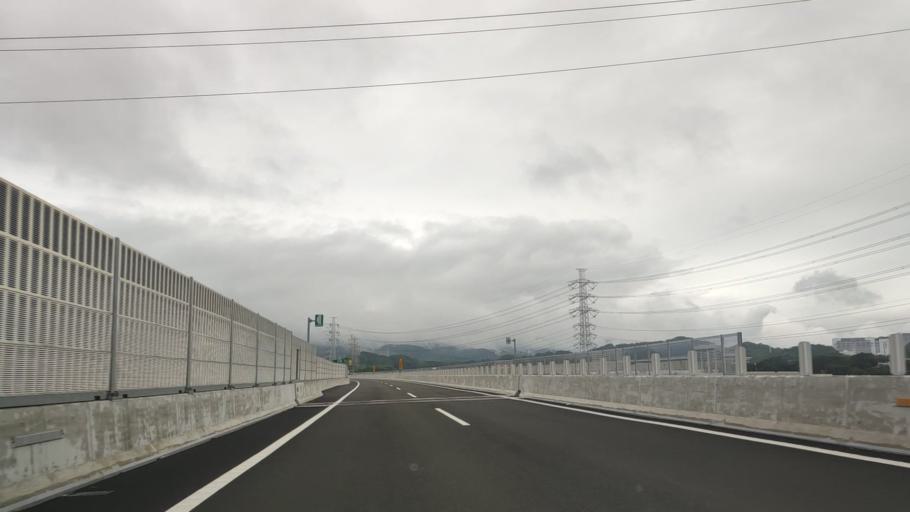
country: JP
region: Kanagawa
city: Isehara
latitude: 35.4067
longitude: 139.3284
